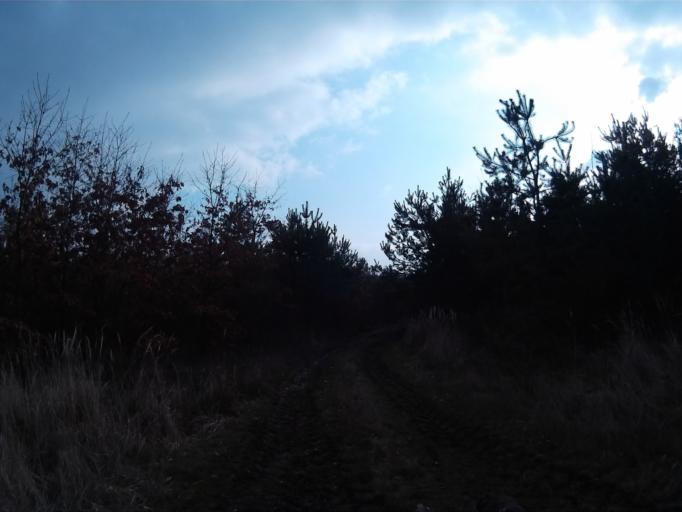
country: HU
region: Vas
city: Sarvar
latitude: 47.1397
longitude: 16.9917
